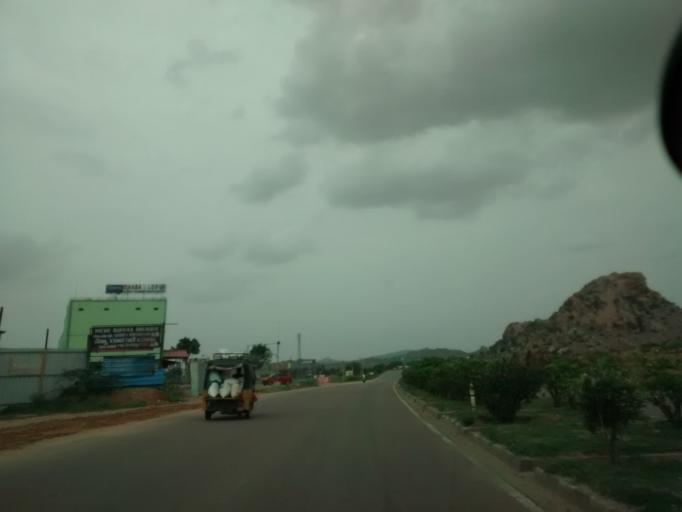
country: IN
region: Andhra Pradesh
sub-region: Kurnool
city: Ramapuram
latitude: 15.1654
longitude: 77.6765
